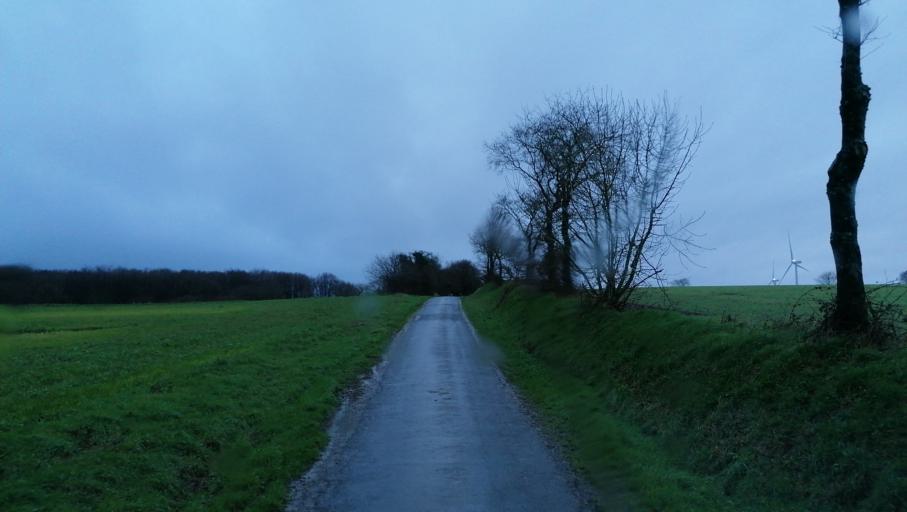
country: FR
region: Brittany
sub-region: Departement des Cotes-d'Armor
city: Lanrodec
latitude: 48.4814
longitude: -2.9988
